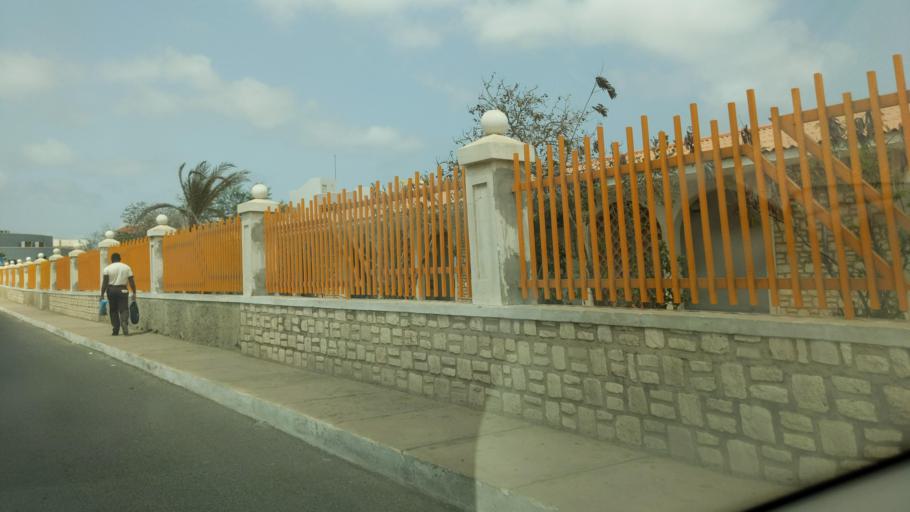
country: CV
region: Sal
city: Espargos
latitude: 16.7533
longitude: -22.9446
